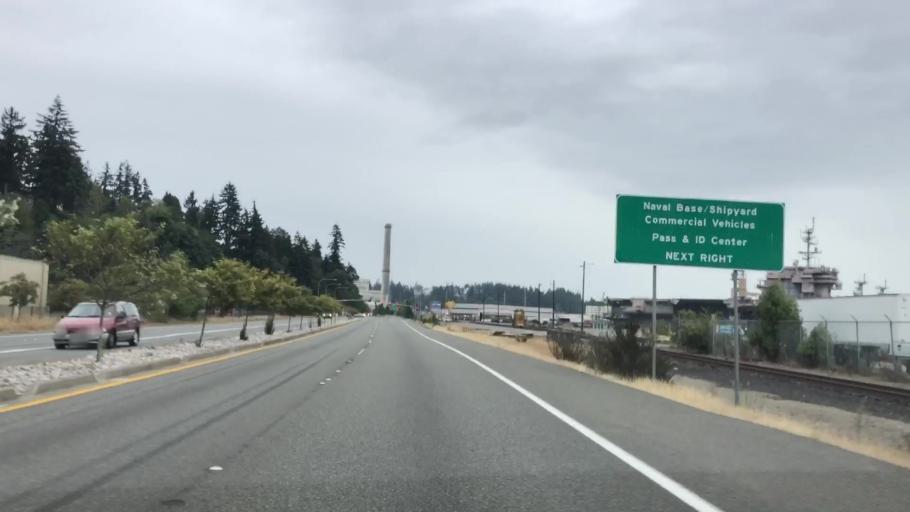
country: US
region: Washington
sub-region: Kitsap County
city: Navy Yard City
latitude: 47.5517
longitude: -122.6621
